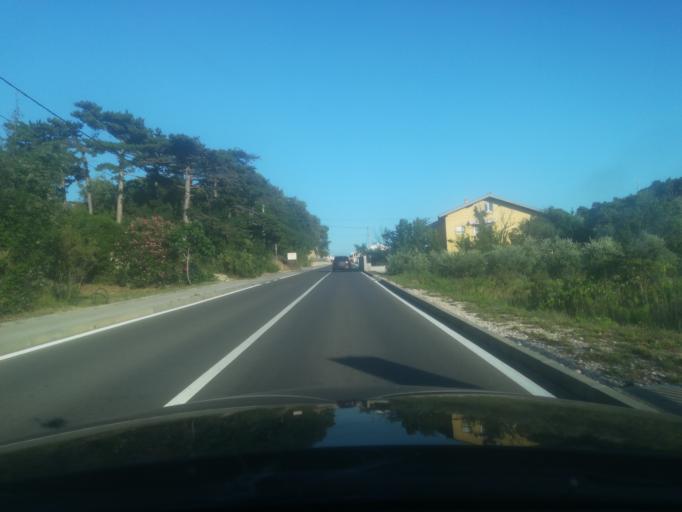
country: HR
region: Primorsko-Goranska
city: Banjol
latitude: 44.7746
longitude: 14.7571
